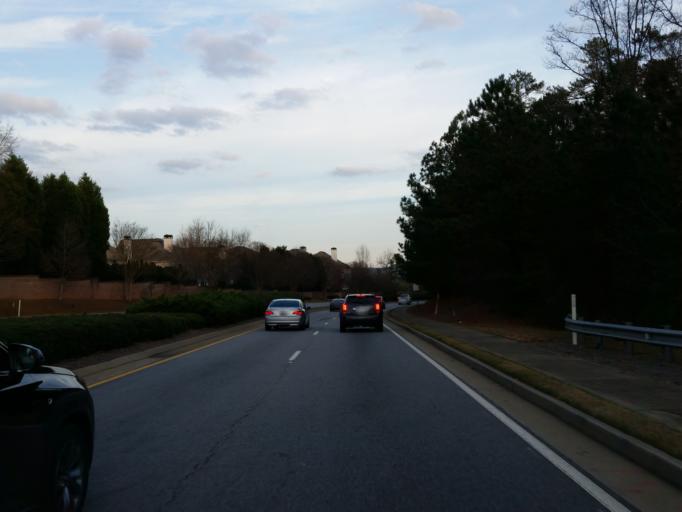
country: US
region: Georgia
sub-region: Cobb County
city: Vinings
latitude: 33.8491
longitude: -84.4890
